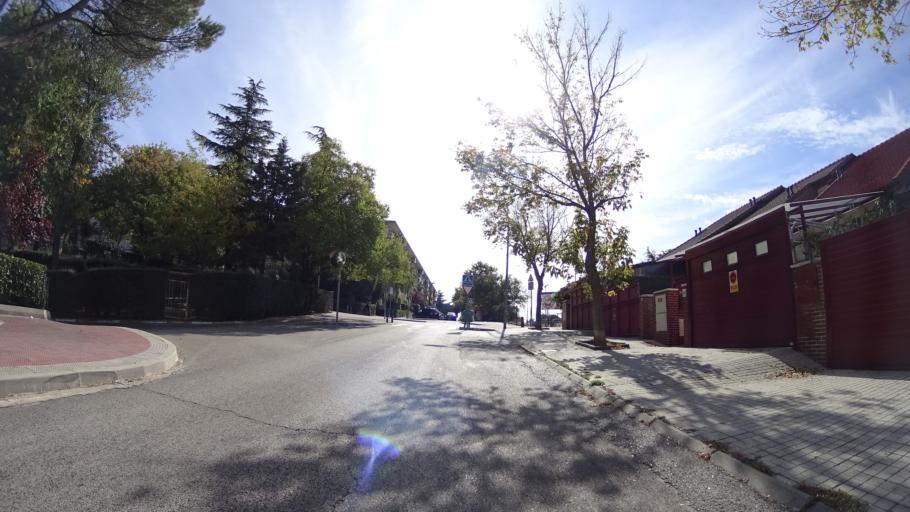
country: ES
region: Madrid
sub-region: Provincia de Madrid
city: Collado-Villalba
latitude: 40.6203
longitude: -4.0137
